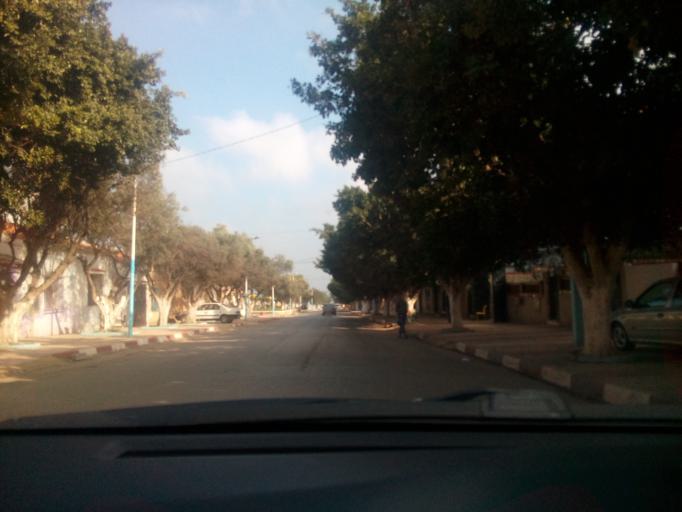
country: DZ
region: Oran
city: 'Ain el Turk
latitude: 35.7029
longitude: -0.8094
